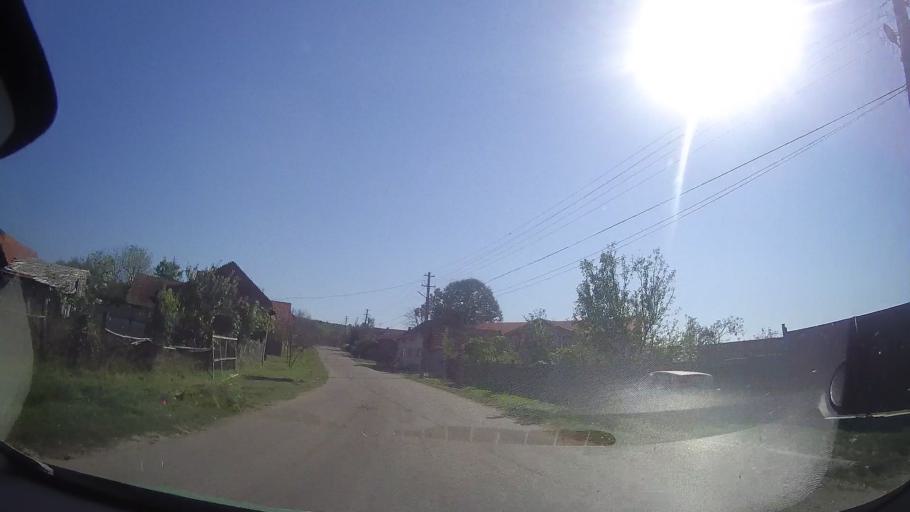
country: RO
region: Timis
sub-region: Comuna Bethausen
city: Bethausen
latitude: 45.8651
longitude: 21.9679
